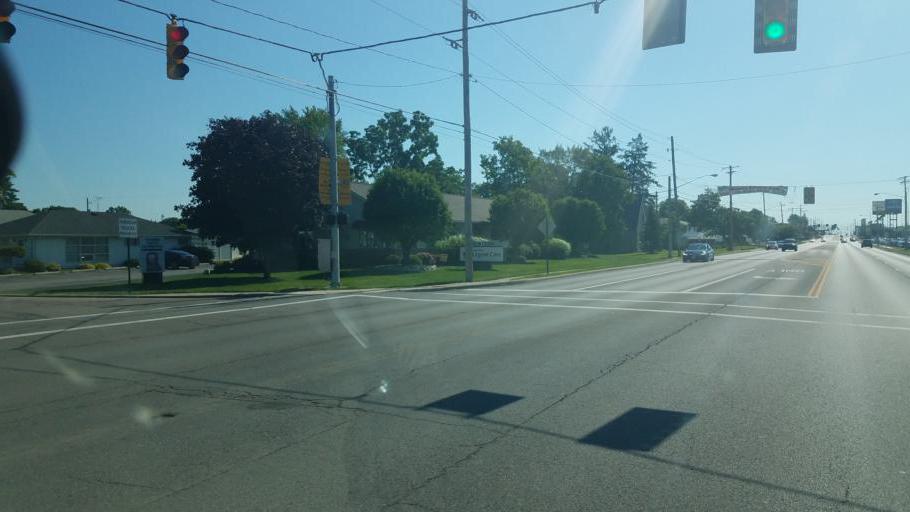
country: US
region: Ohio
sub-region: Marion County
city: Marion
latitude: 40.5806
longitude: -83.1065
